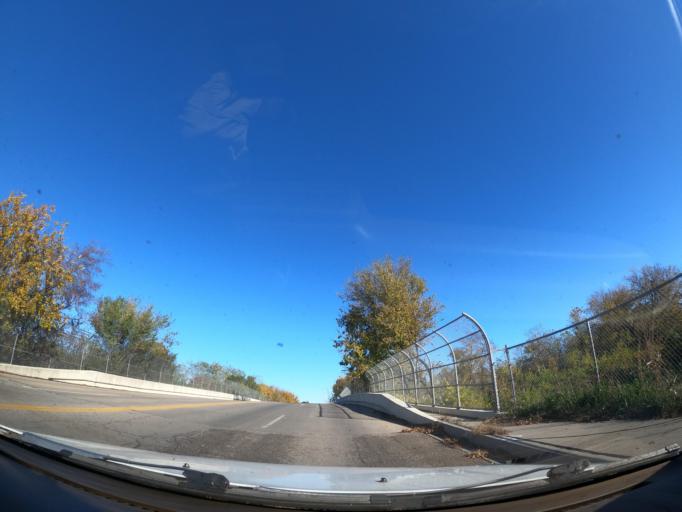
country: US
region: Oklahoma
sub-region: Tulsa County
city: Tulsa
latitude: 36.1647
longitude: -95.9671
